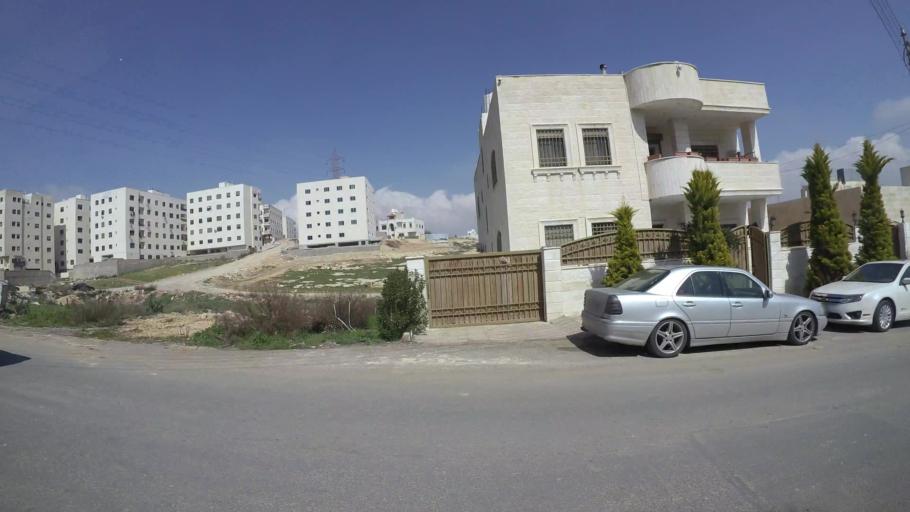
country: JO
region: Amman
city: Al Bunayyat ash Shamaliyah
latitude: 31.8893
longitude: 35.8995
